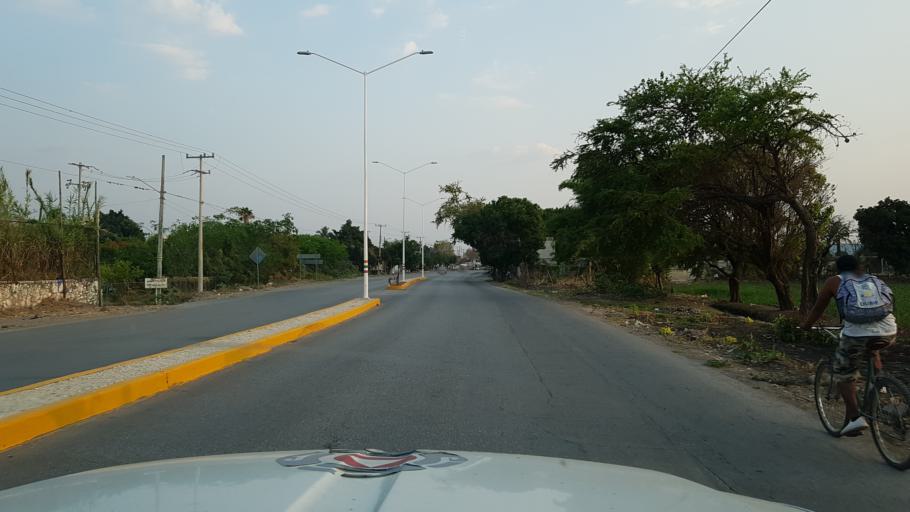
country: MX
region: Morelos
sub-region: Ayala
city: Olintepec
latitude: 18.7453
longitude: -98.9859
